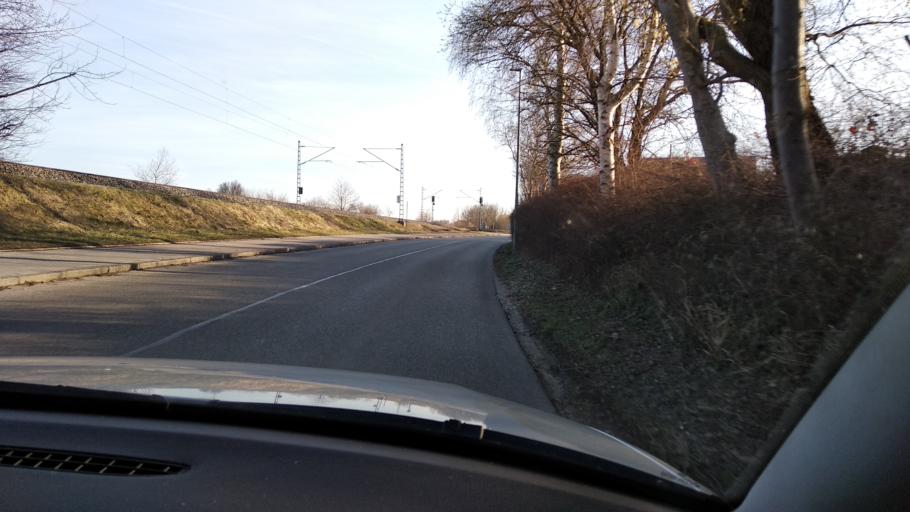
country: DE
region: Bavaria
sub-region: Upper Bavaria
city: Unterhaching
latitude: 48.0585
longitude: 11.6118
